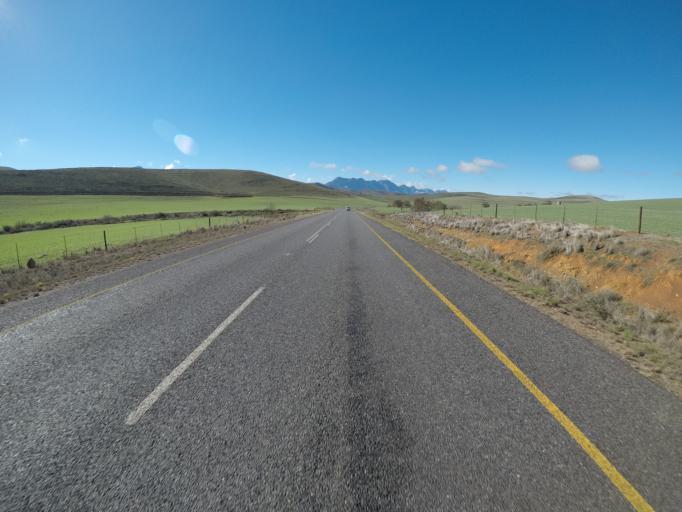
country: ZA
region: Western Cape
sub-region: Overberg District Municipality
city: Caledon
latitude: -34.0948
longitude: 19.5407
